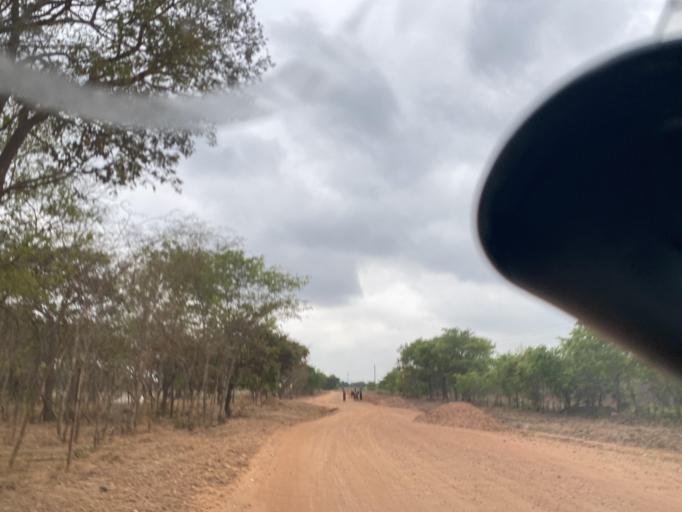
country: ZM
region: Lusaka
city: Chongwe
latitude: -15.2643
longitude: 28.7320
